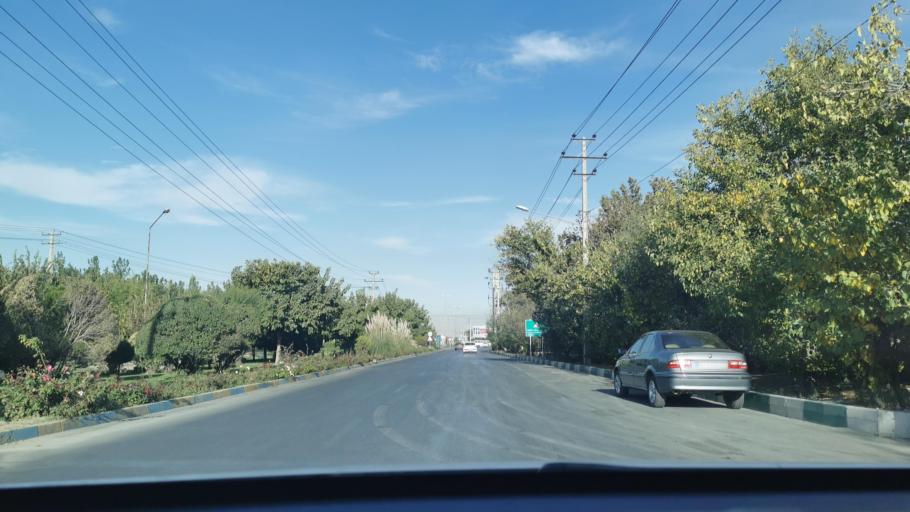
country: IR
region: Razavi Khorasan
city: Torqabeh
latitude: 36.4284
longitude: 59.4163
